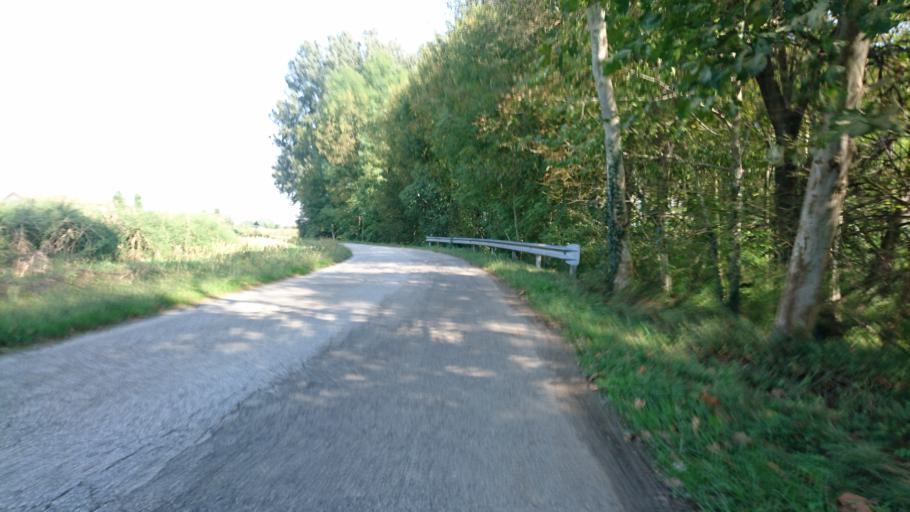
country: IT
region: Veneto
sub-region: Provincia di Padova
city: Piazzola sul Brenta
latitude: 45.5697
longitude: 11.7796
